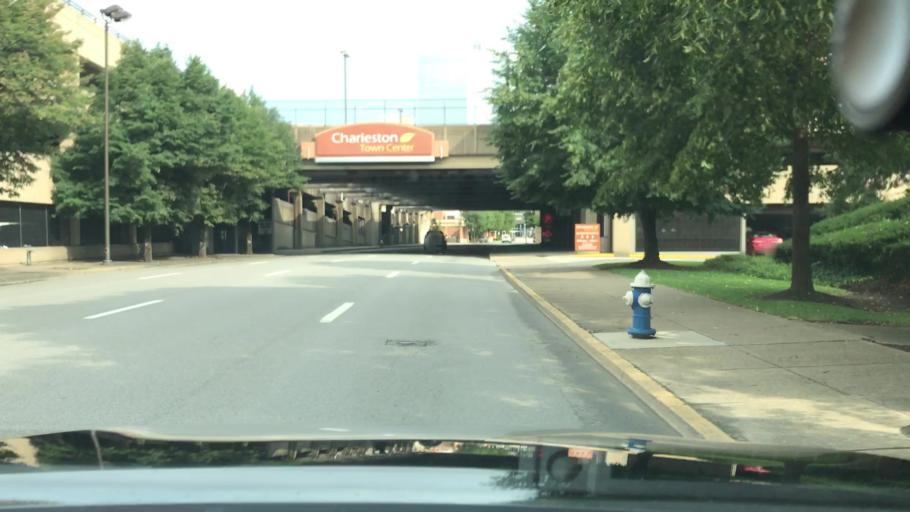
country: US
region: West Virginia
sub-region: Kanawha County
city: Charleston
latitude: 38.3554
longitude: -81.6379
